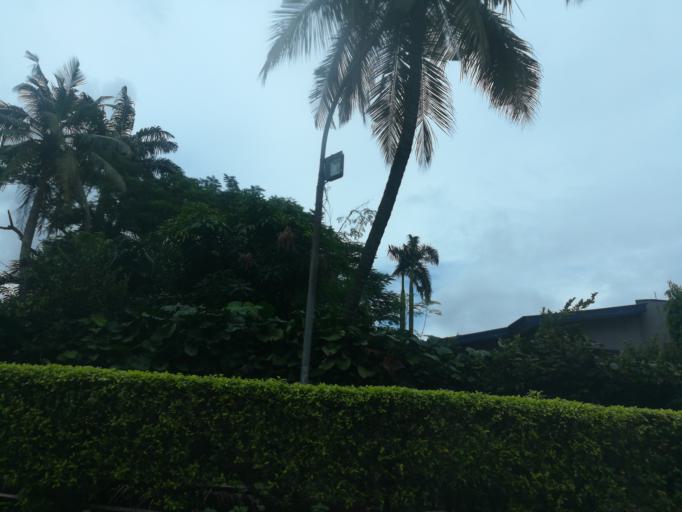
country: NG
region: Lagos
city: Agege
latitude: 6.6210
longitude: 3.3479
